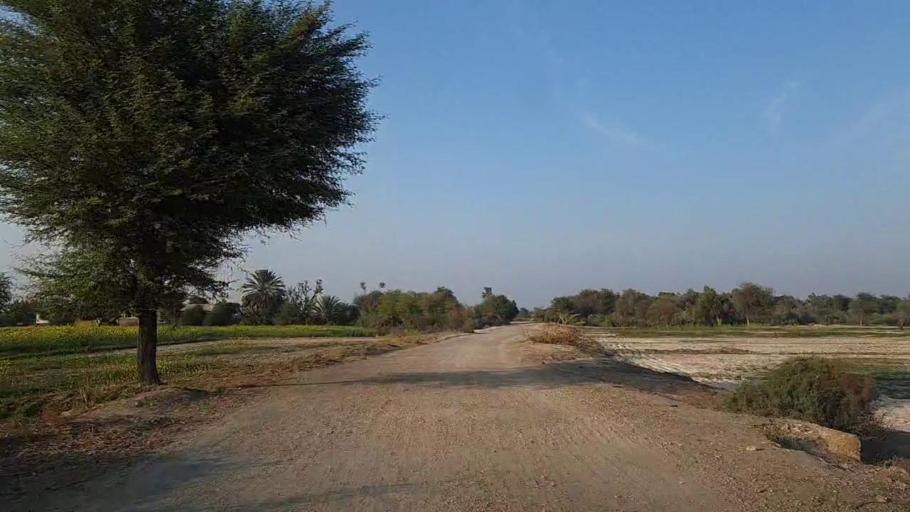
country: PK
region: Sindh
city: Jam Sahib
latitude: 26.3928
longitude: 68.5431
